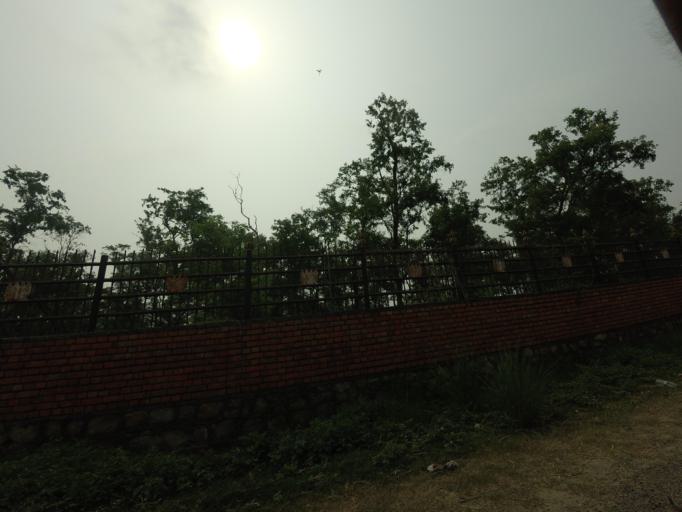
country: IN
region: Uttar Pradesh
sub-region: Maharajganj
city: Nautanwa
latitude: 27.4861
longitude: 83.2680
